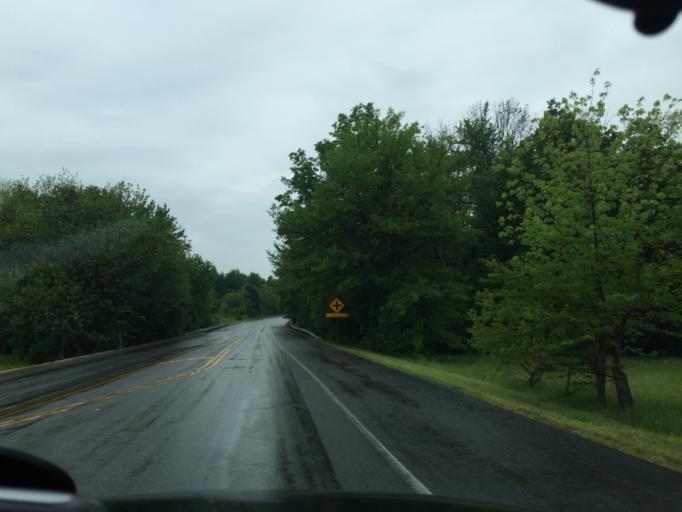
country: US
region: Maryland
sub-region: Washington County
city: Smithsburg
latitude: 39.6476
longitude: -77.5695
